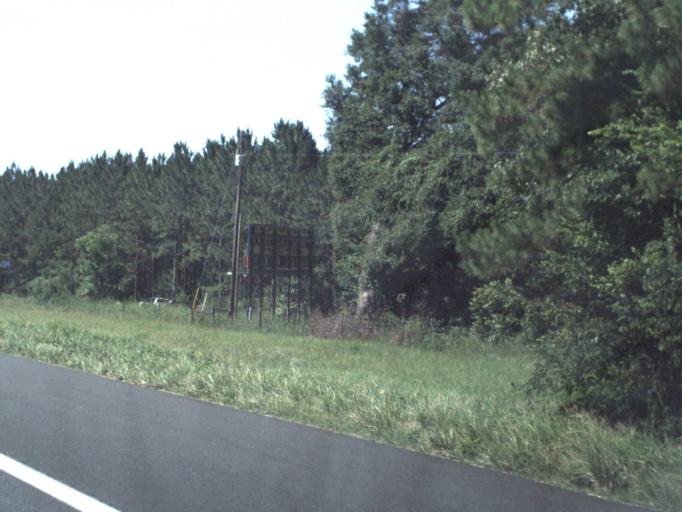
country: US
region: Florida
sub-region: Alachua County
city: Alachua
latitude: 29.7639
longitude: -82.5042
